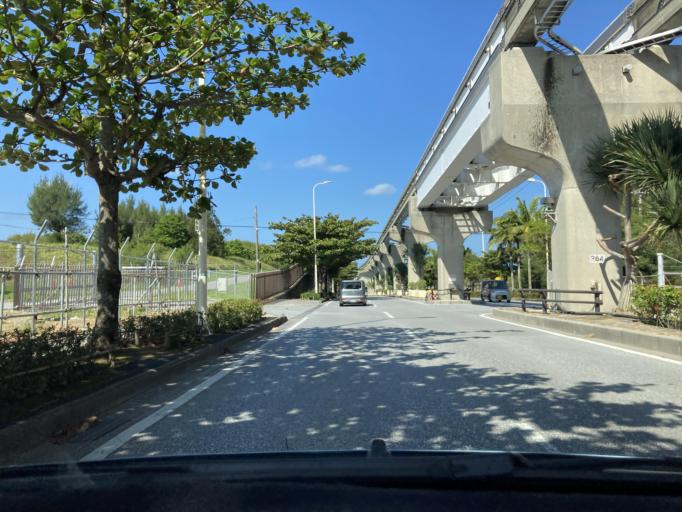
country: JP
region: Okinawa
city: Tomigusuku
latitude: 26.1982
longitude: 127.6592
